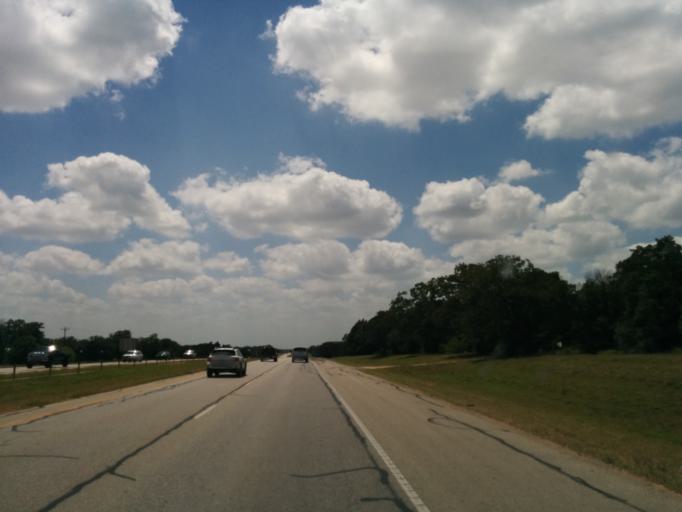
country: US
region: Texas
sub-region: Bastrop County
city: Bastrop
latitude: 30.1109
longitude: -97.3899
